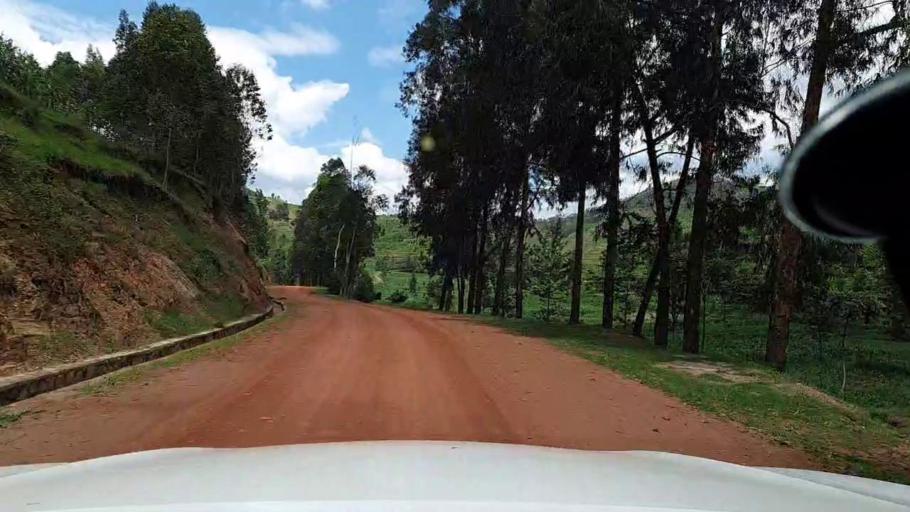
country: RW
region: Northern Province
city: Byumba
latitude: -1.7072
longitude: 29.8490
